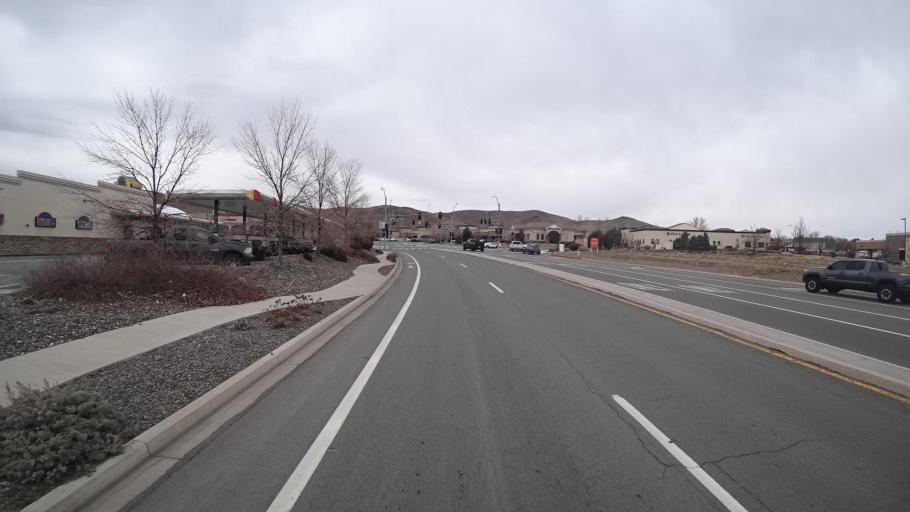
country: US
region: Nevada
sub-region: Washoe County
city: Sun Valley
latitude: 39.5839
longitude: -119.7385
